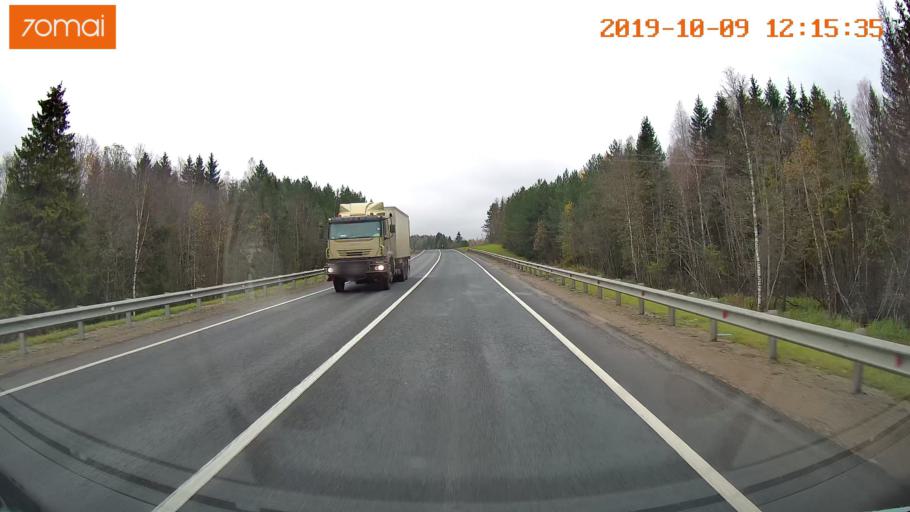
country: RU
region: Jaroslavl
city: Prechistoye
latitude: 58.4813
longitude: 40.3234
